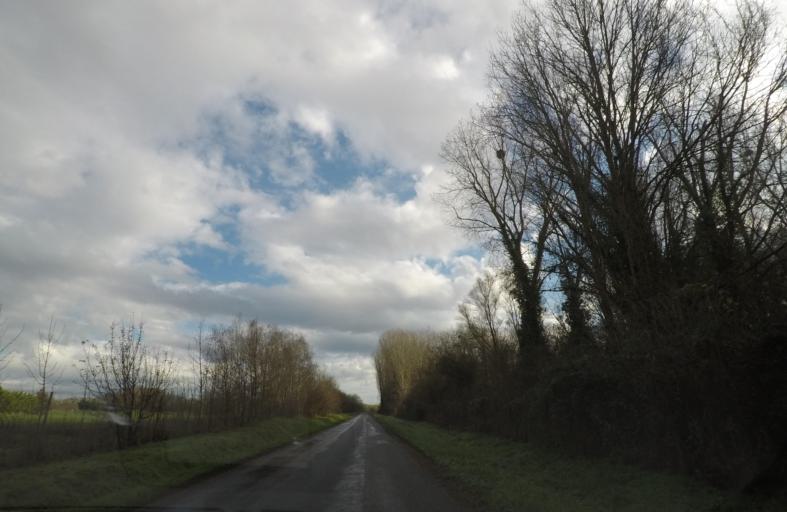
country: FR
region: Centre
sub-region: Departement du Cher
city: Bourges
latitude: 47.0491
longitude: 2.4125
